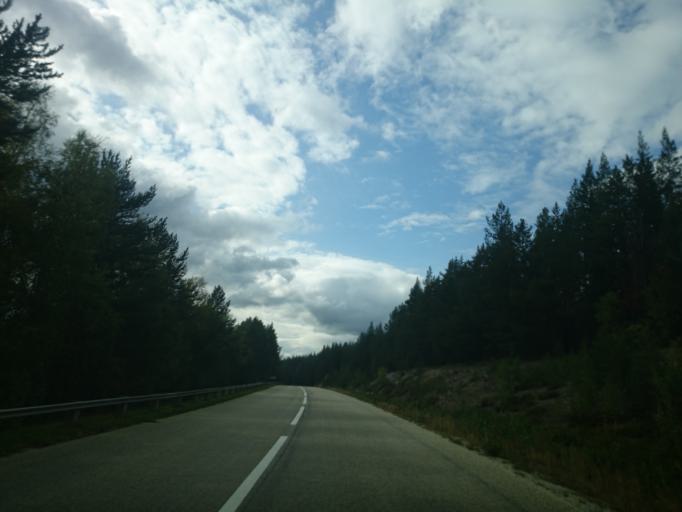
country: SE
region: Jaemtland
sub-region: Harjedalens Kommun
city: Sveg
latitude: 62.4146
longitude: 13.6282
